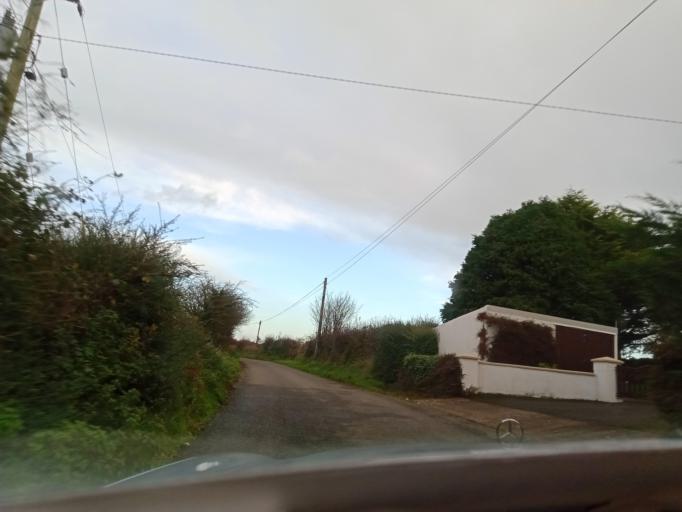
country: IE
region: Munster
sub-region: Waterford
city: Waterford
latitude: 52.3166
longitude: -7.0455
